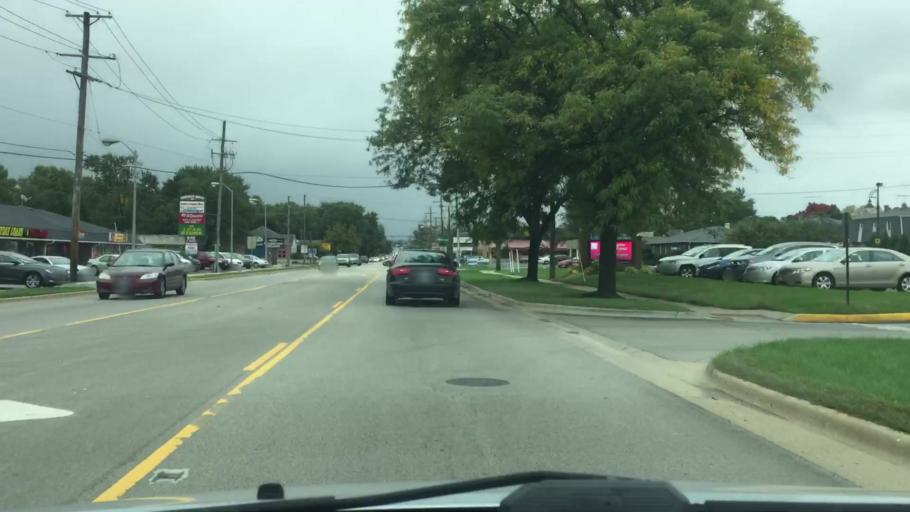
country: US
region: Illinois
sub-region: McHenry County
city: McHenry
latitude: 42.3395
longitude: -88.2747
